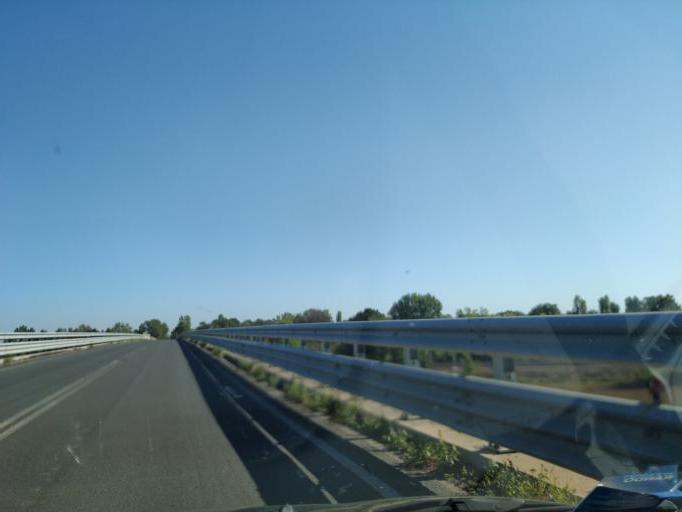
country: IT
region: Emilia-Romagna
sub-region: Provincia di Bologna
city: San Giovanni in Persiceto
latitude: 44.6549
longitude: 11.1798
